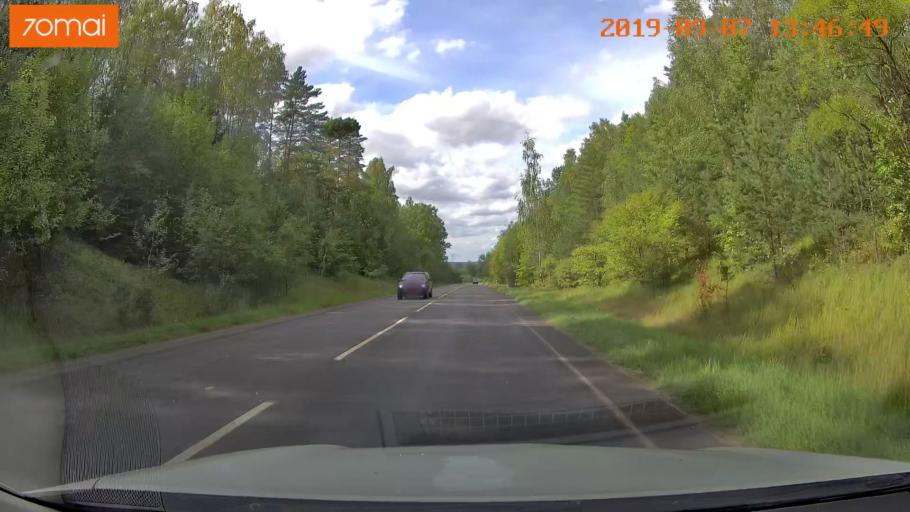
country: LT
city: Baltoji Voke
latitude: 54.5927
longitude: 25.2251
